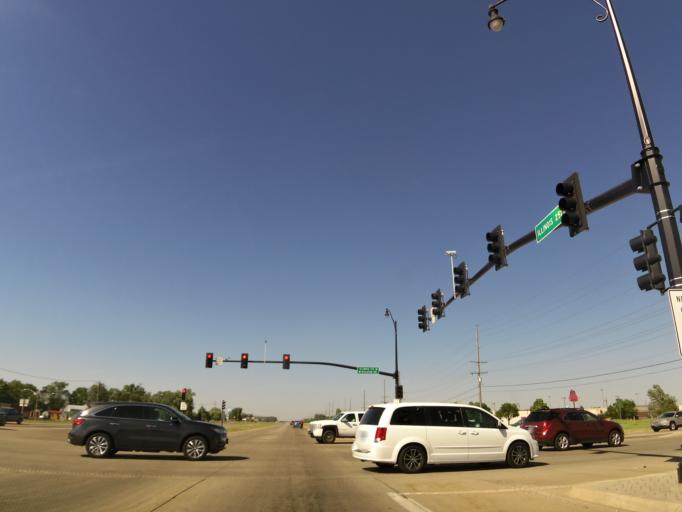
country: US
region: Illinois
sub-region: Winnebago County
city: Machesney Park
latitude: 42.3660
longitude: -89.0353
